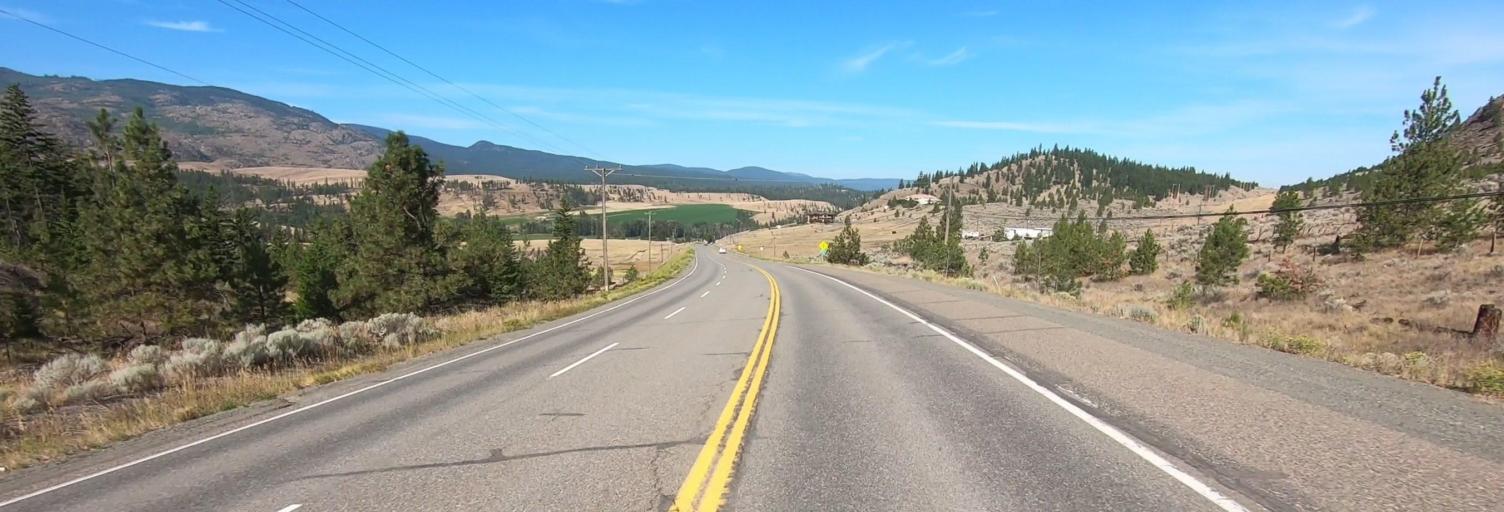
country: CA
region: British Columbia
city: Kamloops
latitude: 50.6617
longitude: -120.5413
